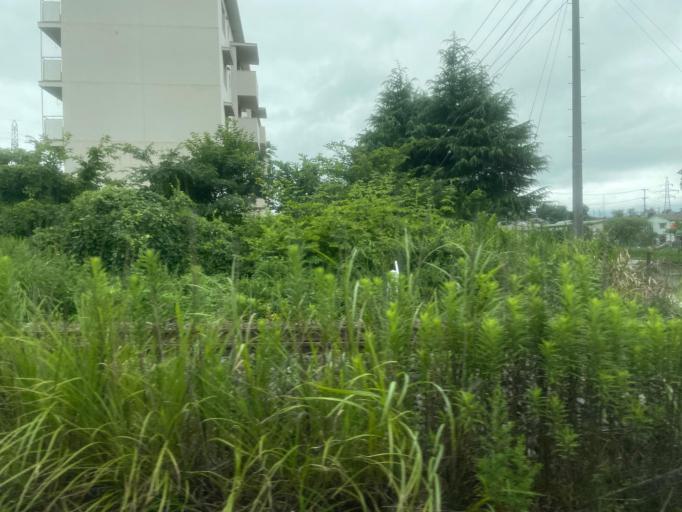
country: JP
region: Fukushima
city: Motomiya
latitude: 37.5044
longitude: 140.3997
